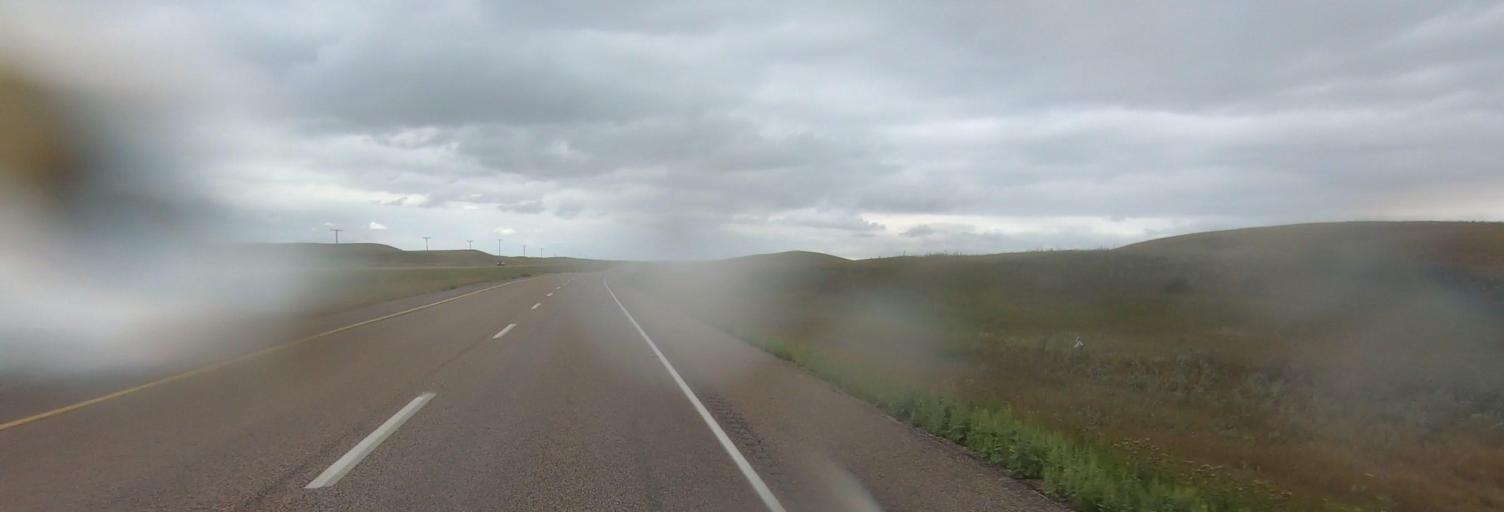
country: CA
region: Saskatchewan
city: Gravelbourg
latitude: 50.4630
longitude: -106.4757
